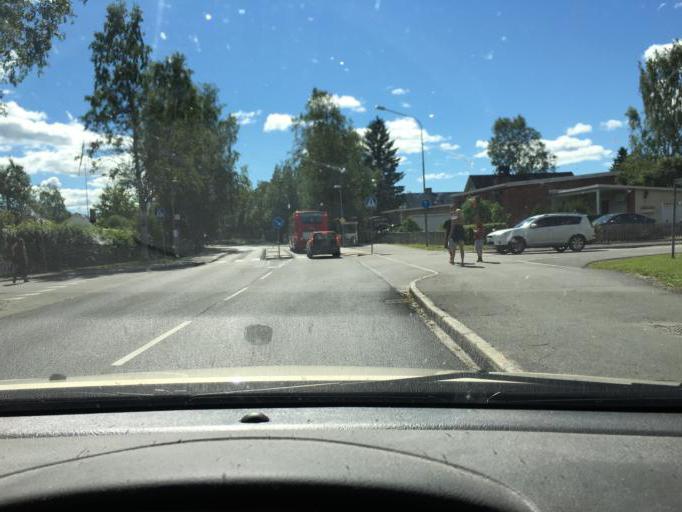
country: SE
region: Norrbotten
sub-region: Lulea Kommun
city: Lulea
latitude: 65.5977
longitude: 22.1348
